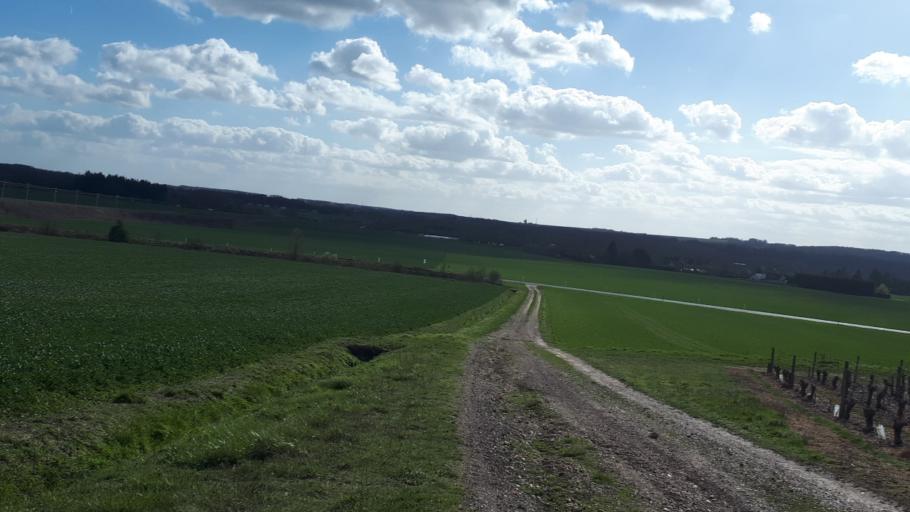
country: FR
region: Centre
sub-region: Departement du Loir-et-Cher
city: Villiers-sur-Loir
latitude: 47.7993
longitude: 1.0077
